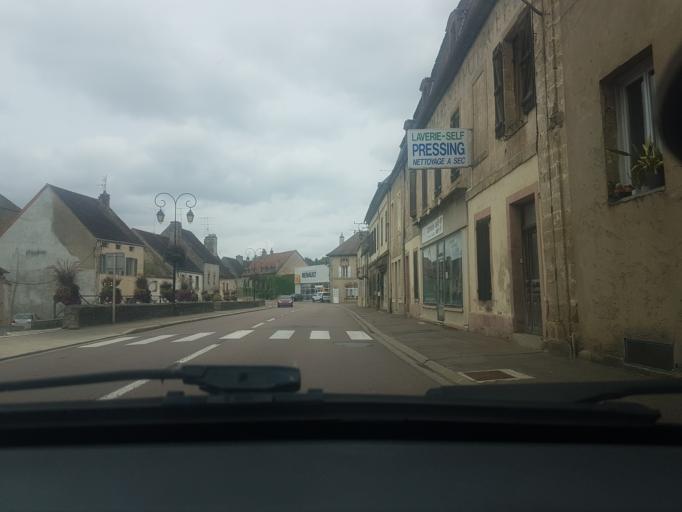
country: FR
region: Bourgogne
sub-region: Departement de la Cote-d'Or
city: Arnay-le-Duc
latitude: 47.1353
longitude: 4.4856
